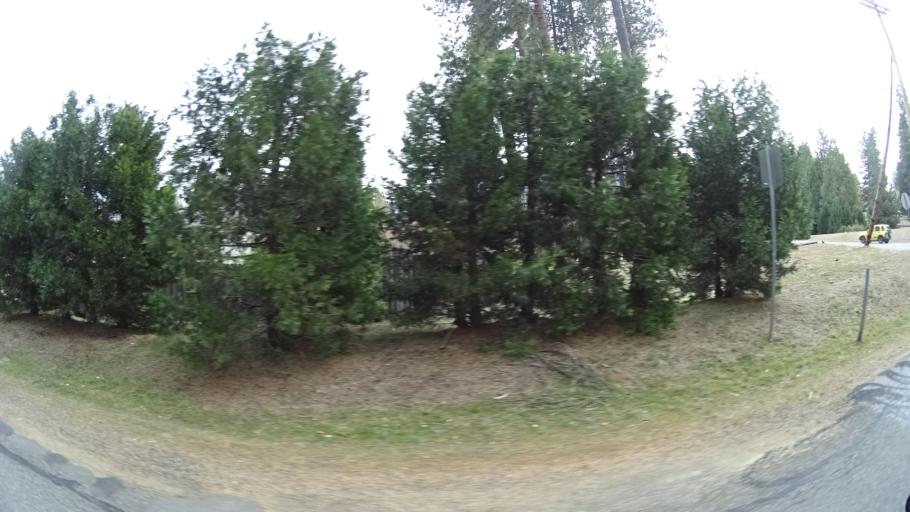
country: US
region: California
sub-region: Siskiyou County
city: Weed
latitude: 41.4016
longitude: -122.3803
